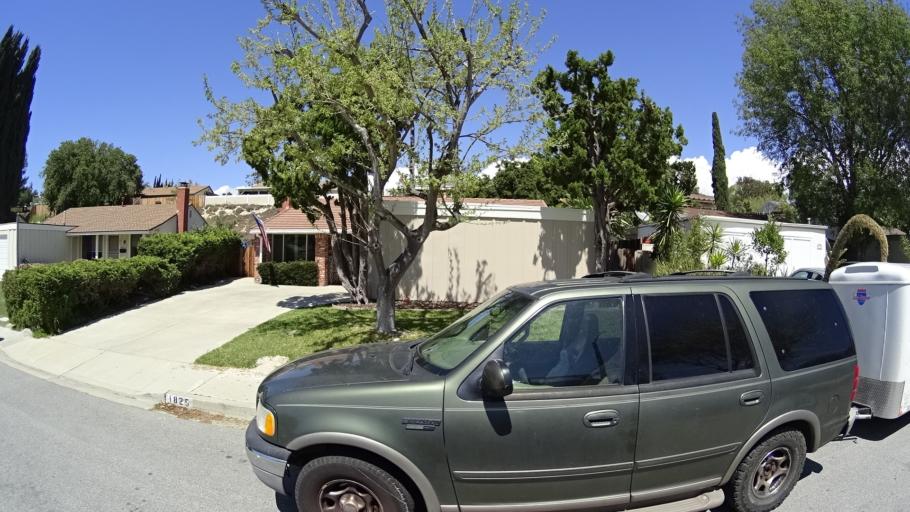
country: US
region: California
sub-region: Ventura County
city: Thousand Oaks
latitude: 34.2133
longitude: -118.8450
